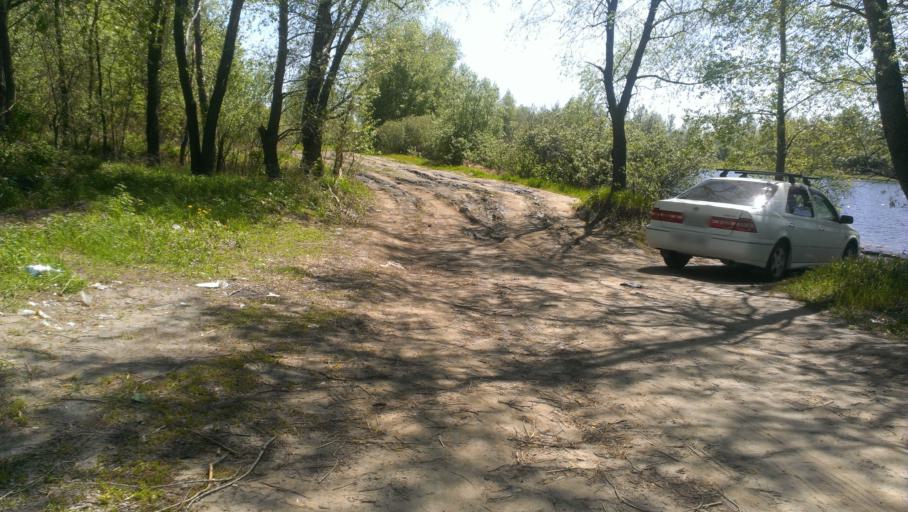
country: RU
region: Altai Krai
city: Zaton
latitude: 53.3145
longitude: 83.8509
